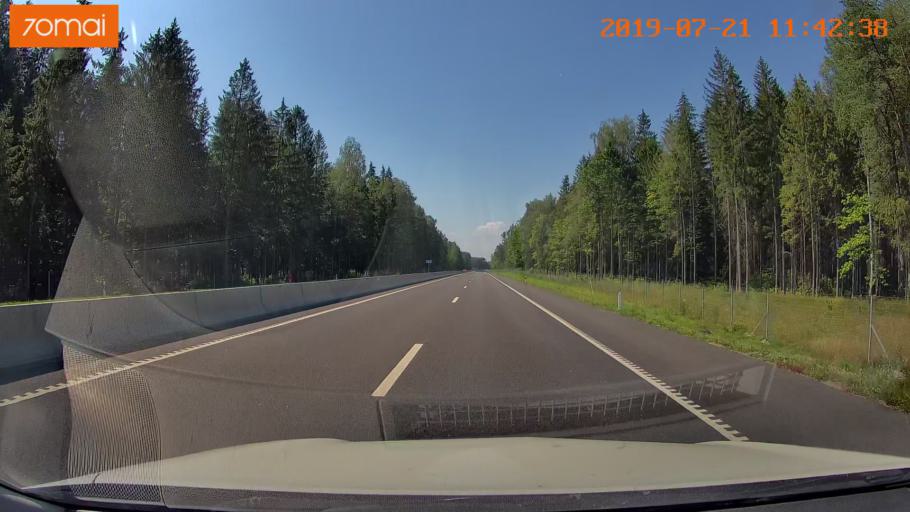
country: BY
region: Grodnenskaya
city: Lyubcha
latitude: 53.9316
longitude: 26.1310
